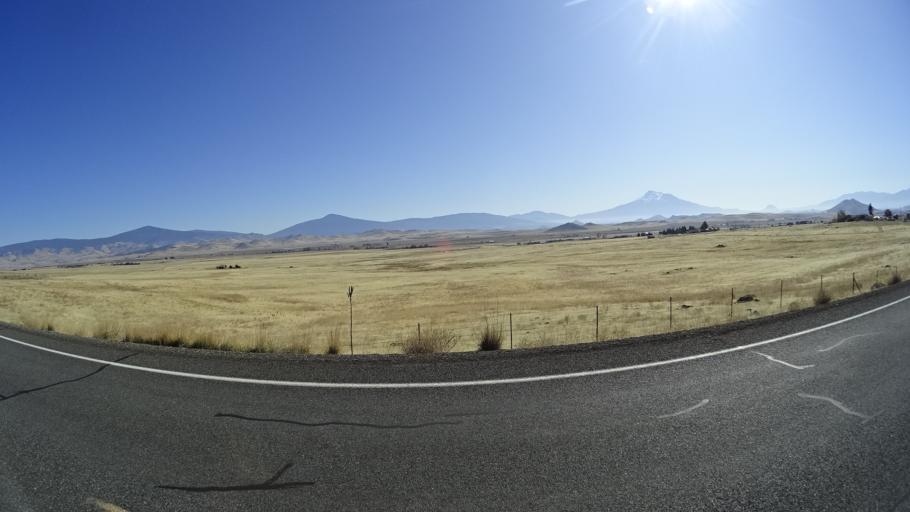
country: US
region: California
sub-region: Siskiyou County
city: Montague
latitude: 41.7775
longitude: -122.5238
